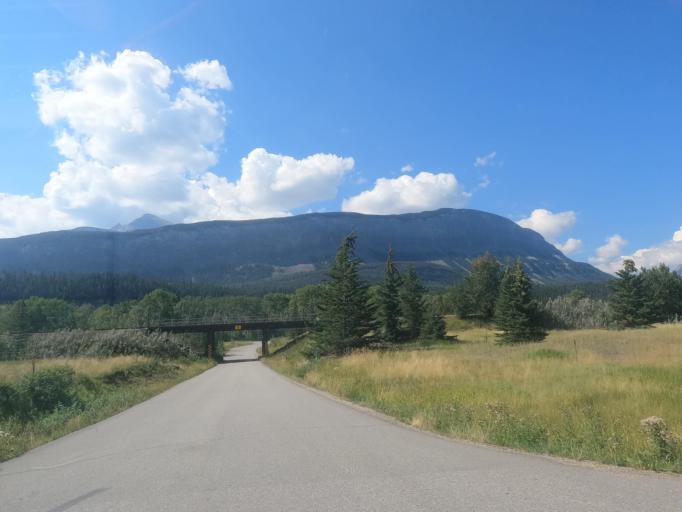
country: CA
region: Alberta
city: Jasper Park Lodge
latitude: 52.9711
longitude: -118.0573
